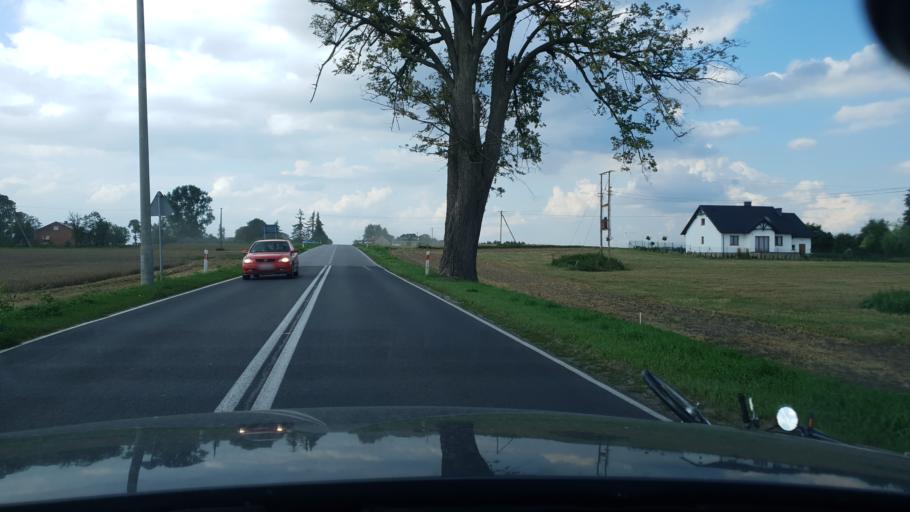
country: PL
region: Kujawsko-Pomorskie
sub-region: Powiat wabrzeski
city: Wabrzezno
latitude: 53.3095
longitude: 18.9349
